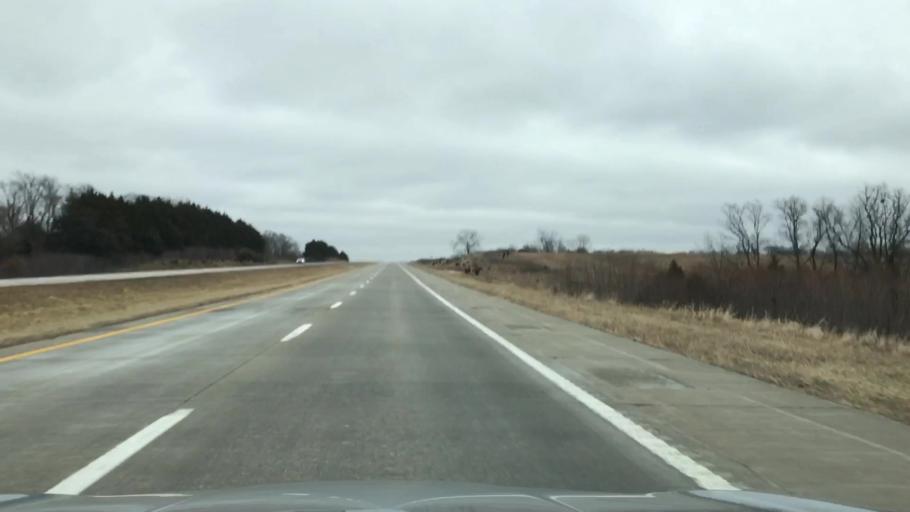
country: US
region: Missouri
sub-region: Caldwell County
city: Hamilton
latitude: 39.7351
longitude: -93.8630
